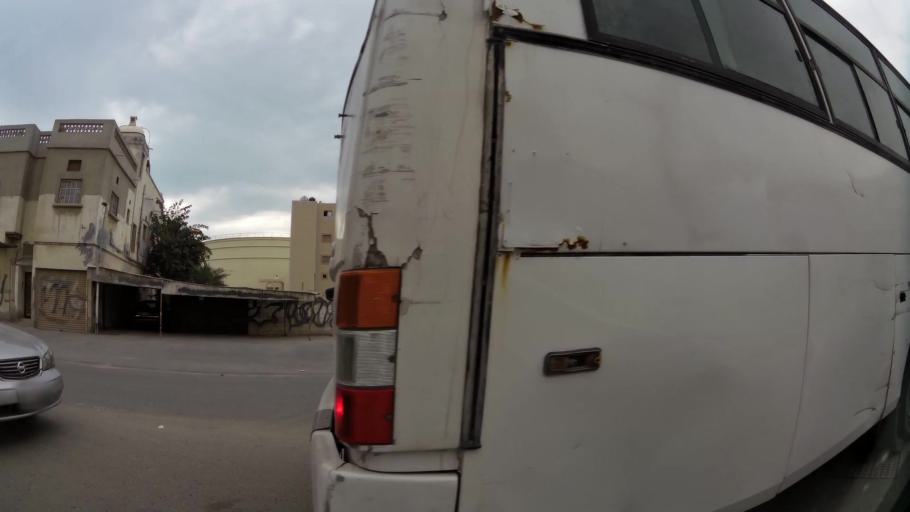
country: BH
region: Northern
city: Sitrah
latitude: 26.1654
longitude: 50.6082
